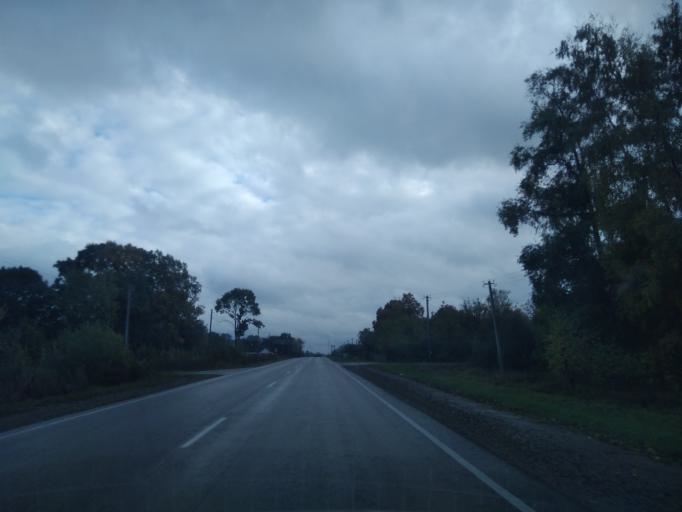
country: RU
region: Tula
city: Yefremov
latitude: 53.2399
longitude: 37.9768
